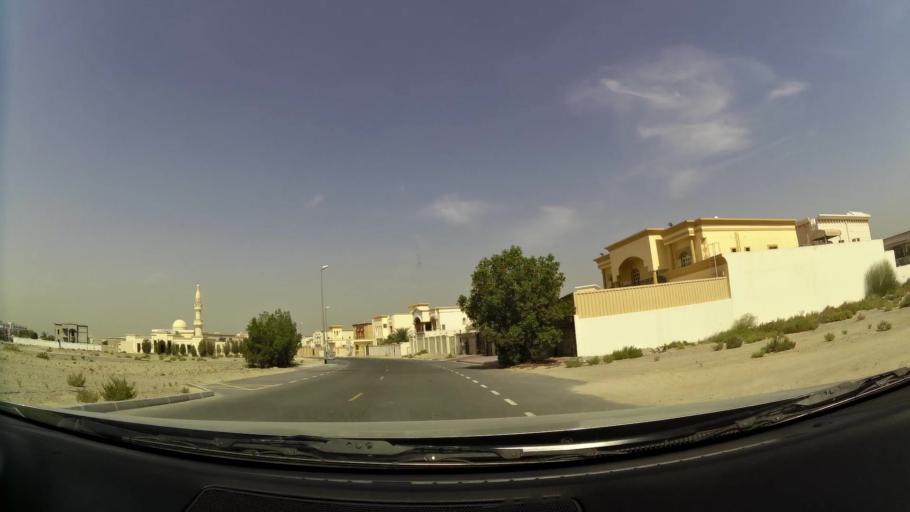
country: AE
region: Ash Shariqah
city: Sharjah
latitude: 25.1998
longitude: 55.4296
